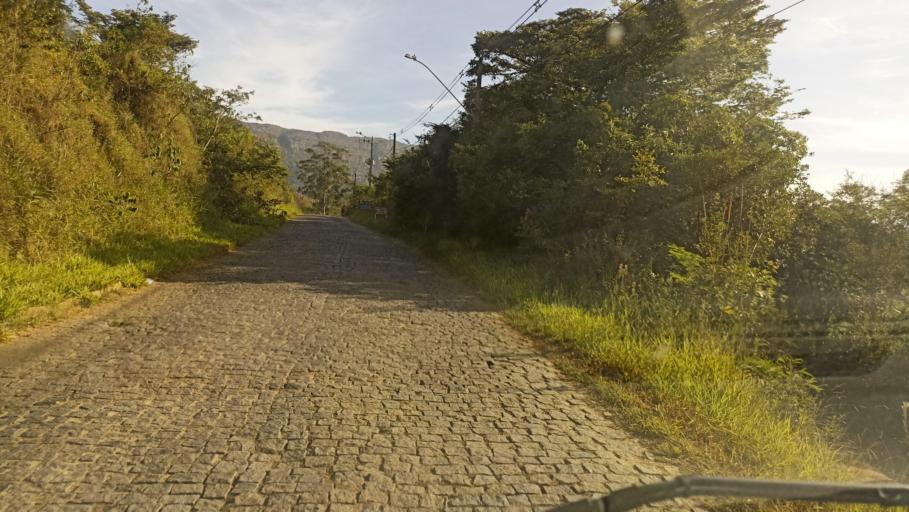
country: BR
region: Minas Gerais
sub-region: Tiradentes
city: Tiradentes
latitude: -21.1206
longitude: -44.1898
